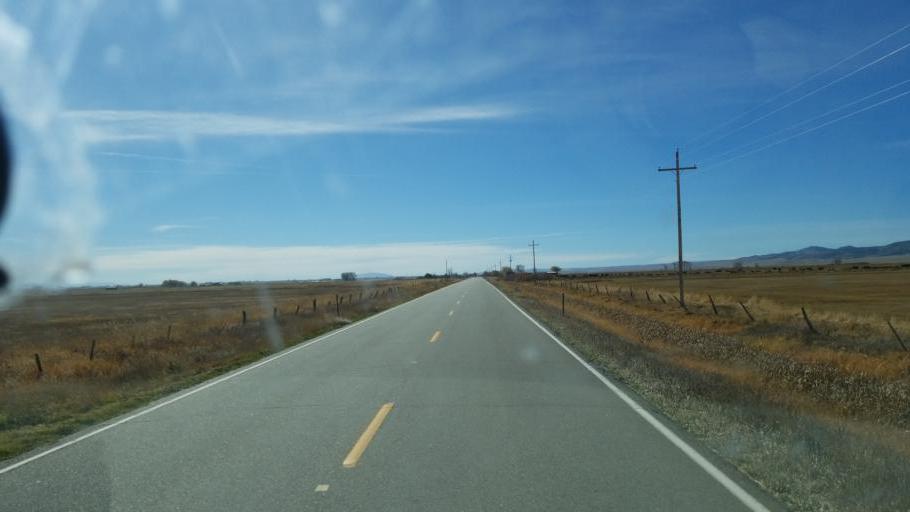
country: US
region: Colorado
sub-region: Rio Grande County
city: Monte Vista
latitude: 37.5190
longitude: -106.1493
